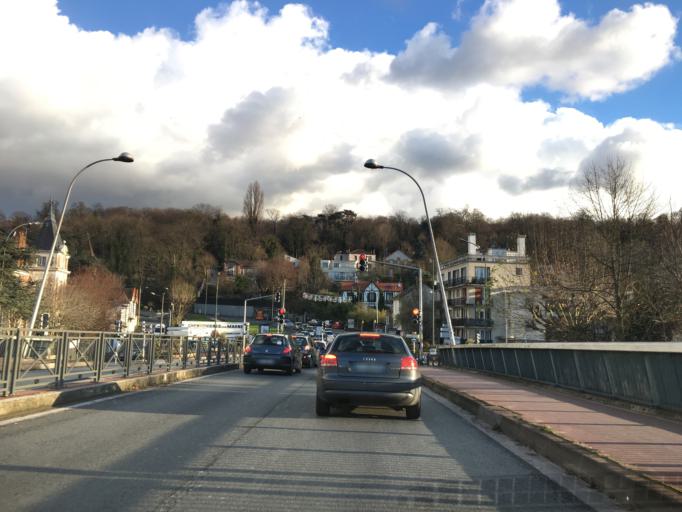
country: FR
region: Ile-de-France
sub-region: Departement du Val-de-Marne
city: Chennevieres-sur-Marne
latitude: 48.7905
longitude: 2.5218
